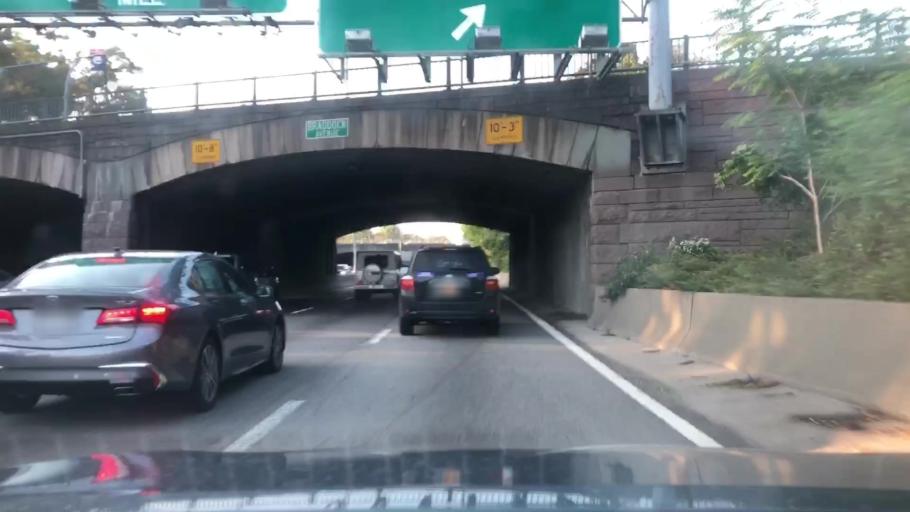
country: US
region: New York
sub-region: Nassau County
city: Bellerose Terrace
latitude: 40.7258
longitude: -73.7245
